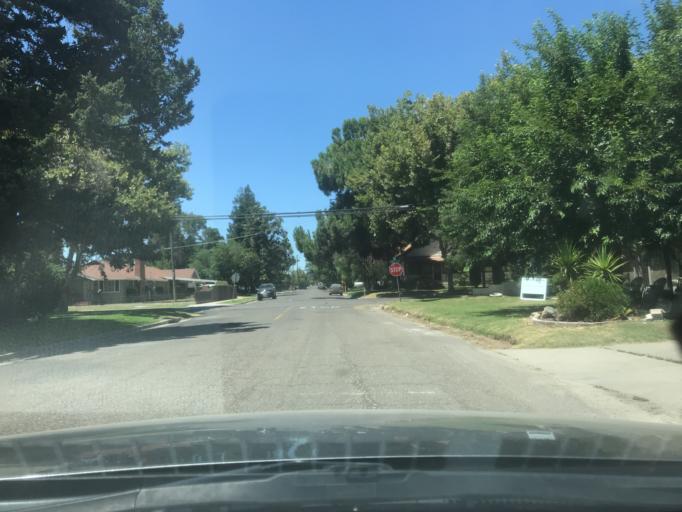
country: US
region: California
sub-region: Merced County
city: Atwater
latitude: 37.3489
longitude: -120.6048
